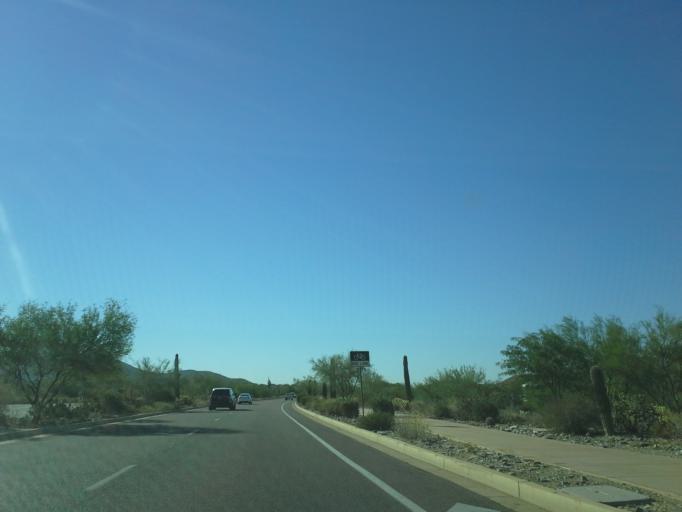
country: US
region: Arizona
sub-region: Maricopa County
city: Paradise Valley
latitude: 33.6477
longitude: -111.8626
